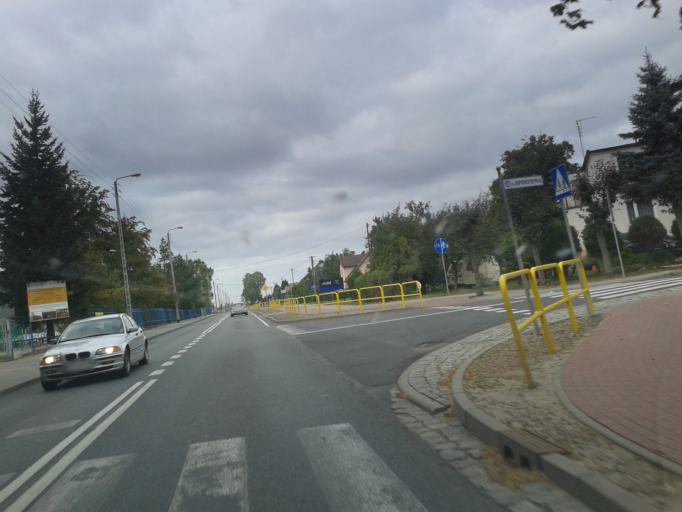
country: PL
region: Kujawsko-Pomorskie
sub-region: Powiat sepolenski
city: Sepolno Krajenskie
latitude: 53.4606
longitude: 17.5316
